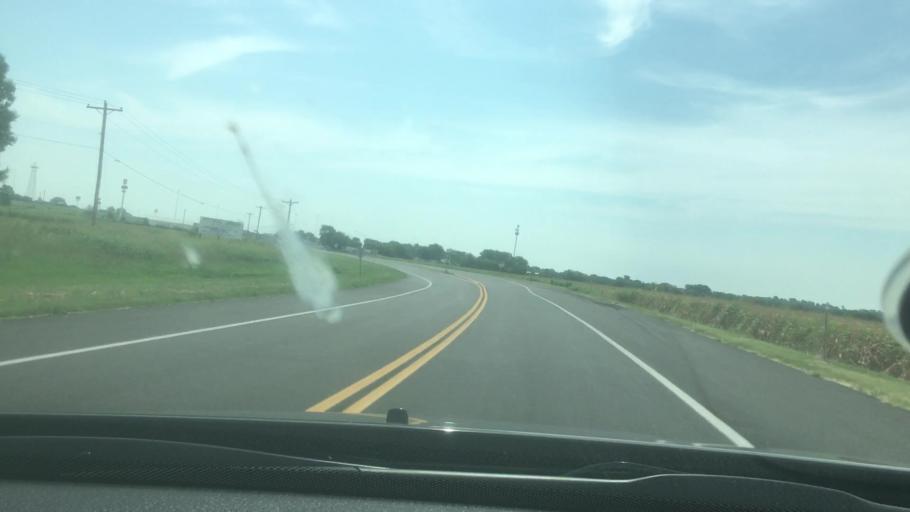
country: US
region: Oklahoma
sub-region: Garvin County
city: Pauls Valley
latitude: 34.7399
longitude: -97.2754
